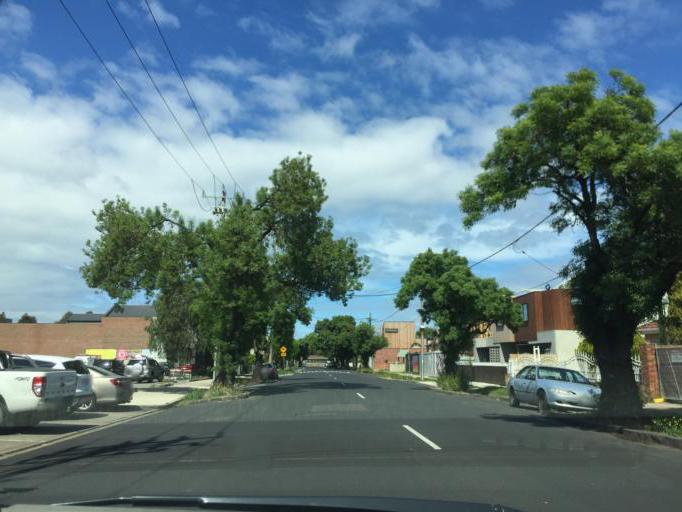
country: AU
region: Victoria
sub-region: Maribyrnong
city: West Footscray
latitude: -37.7982
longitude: 144.8798
